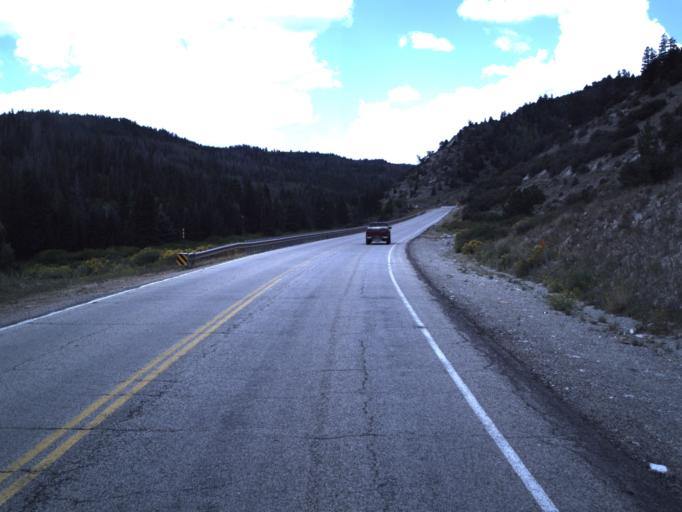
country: US
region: Utah
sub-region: Carbon County
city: Helper
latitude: 39.9068
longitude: -110.7091
